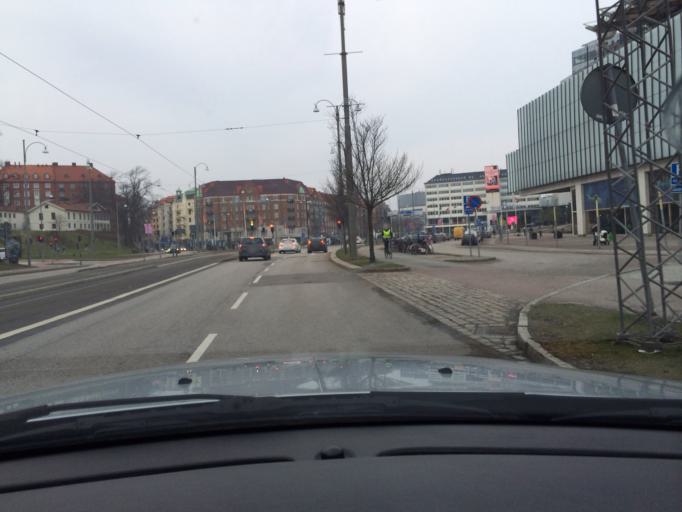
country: SE
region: Vaestra Goetaland
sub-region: Goteborg
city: Goeteborg
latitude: 57.6951
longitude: 11.9884
